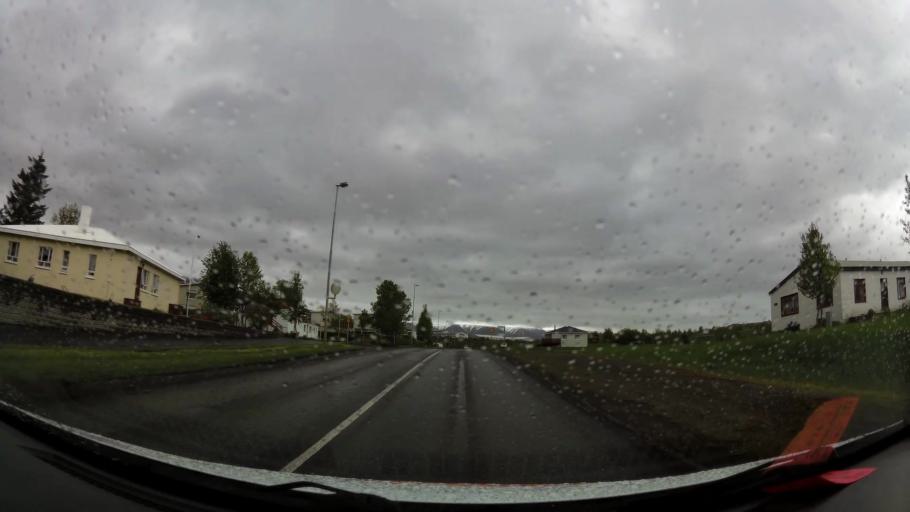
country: IS
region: Northeast
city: Akureyri
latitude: 65.6949
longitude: -18.1097
